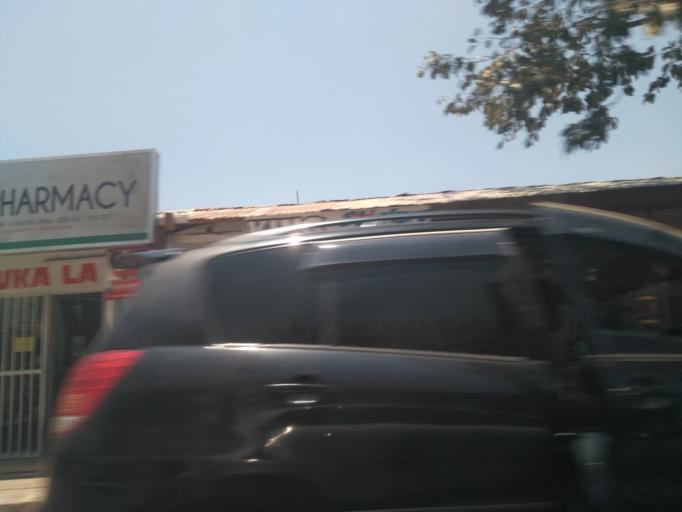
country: TZ
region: Dodoma
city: Dodoma
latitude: -6.1760
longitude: 35.7451
